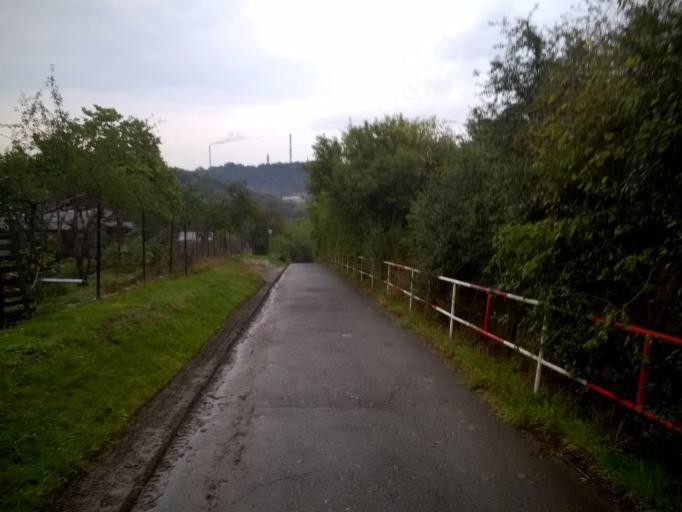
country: CZ
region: Praha
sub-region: Praha 9
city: Vysocany
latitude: 50.0968
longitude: 14.5070
